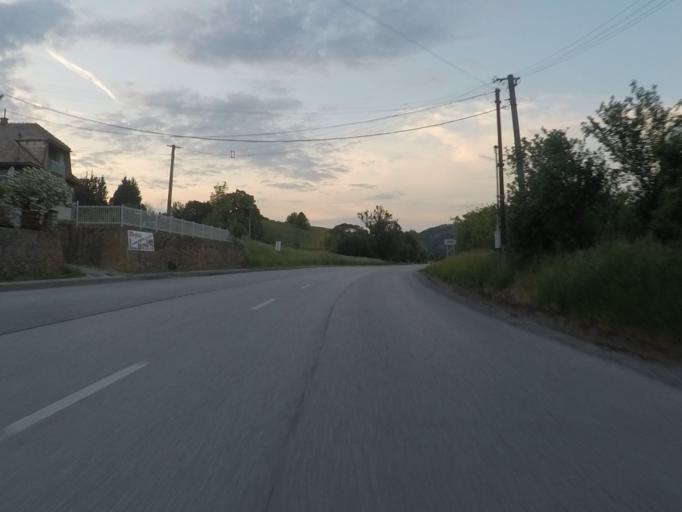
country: SK
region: Banskobystricky
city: Rimavska Sobota
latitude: 48.4803
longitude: 19.9444
